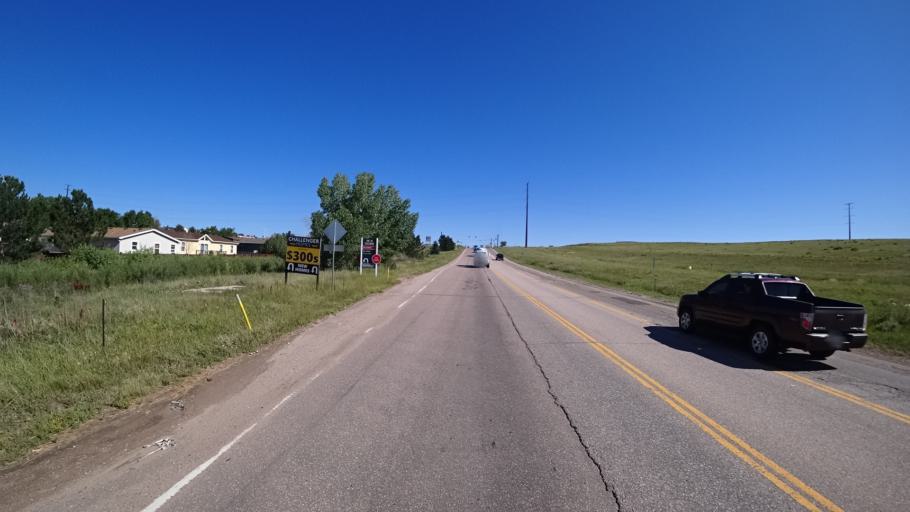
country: US
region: Colorado
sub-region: El Paso County
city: Cimarron Hills
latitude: 38.8988
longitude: -104.6829
